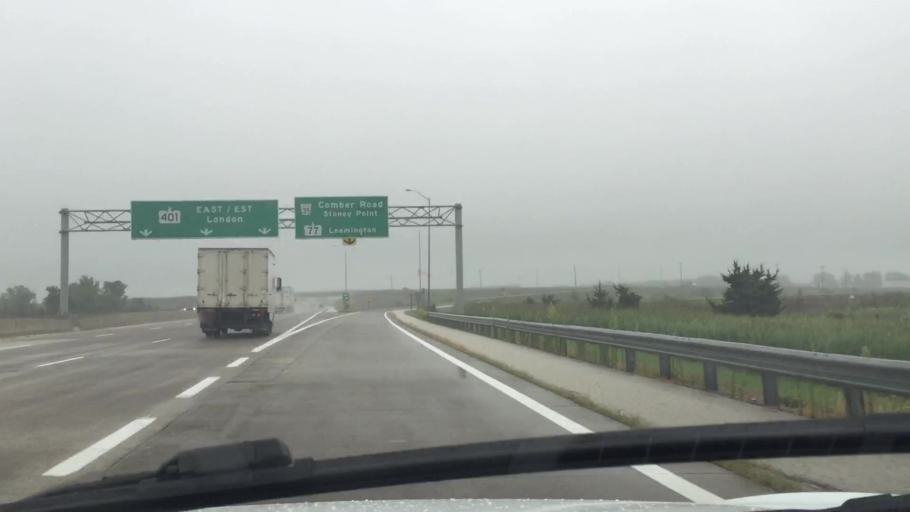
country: US
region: Michigan
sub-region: Wayne County
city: Grosse Pointe Farms
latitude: 42.2424
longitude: -82.5579
